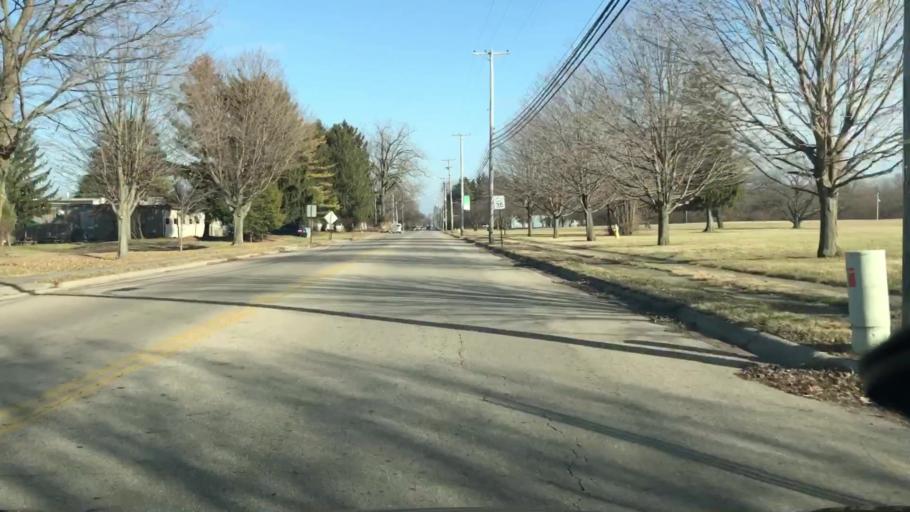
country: US
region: Ohio
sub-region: Greene County
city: Yellow Springs
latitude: 39.8029
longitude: -83.9073
